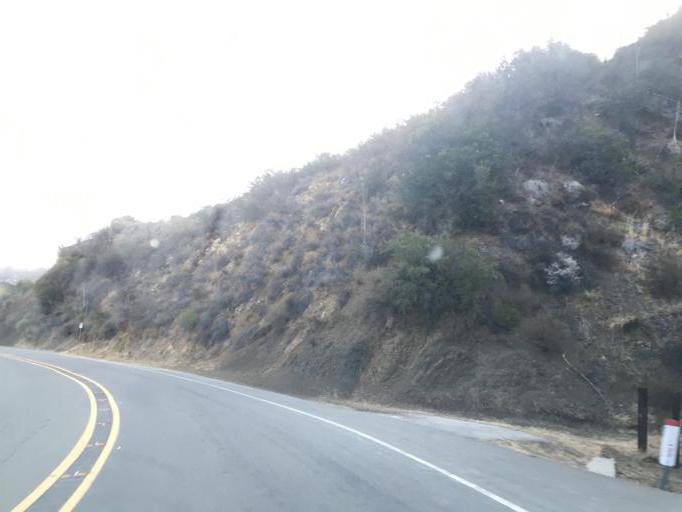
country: US
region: California
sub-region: Los Angeles County
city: Malibu Beach
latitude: 34.0902
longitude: -118.6804
